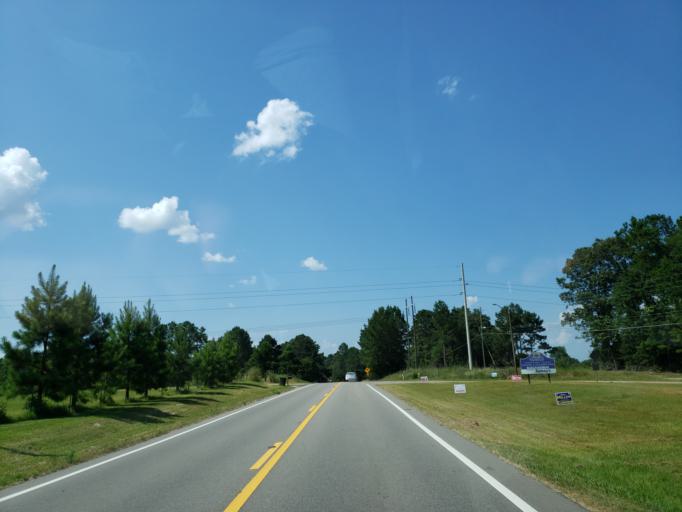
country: US
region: Mississippi
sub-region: Lamar County
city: Sumrall
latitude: 31.3980
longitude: -89.5420
